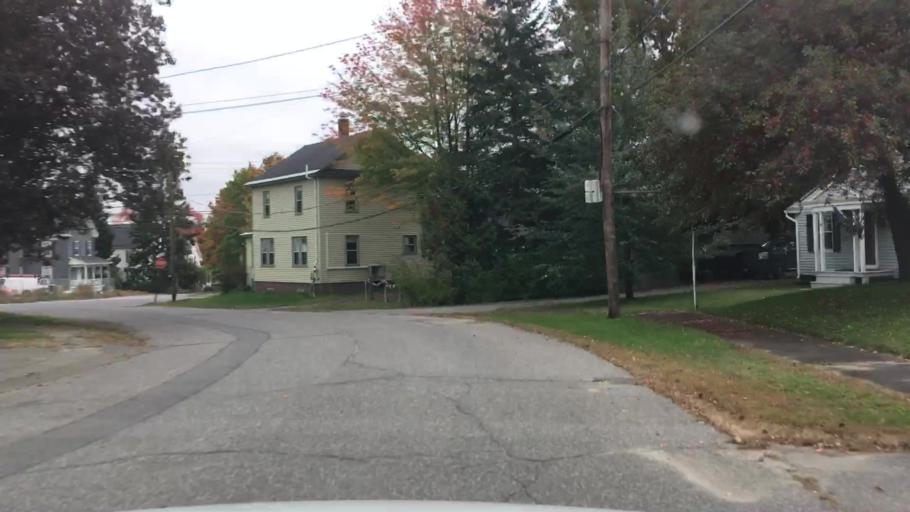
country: US
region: Maine
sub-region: Kennebec County
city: Waterville
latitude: 44.5615
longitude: -69.6357
